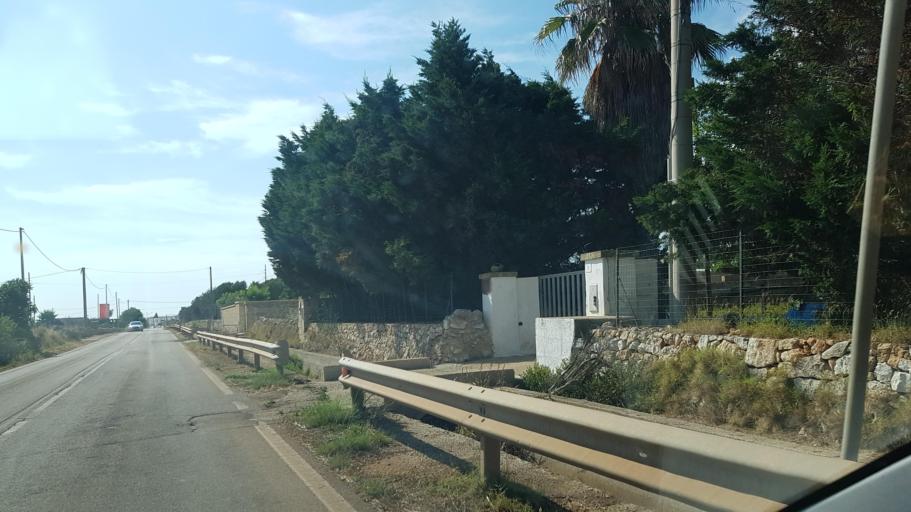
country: IT
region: Apulia
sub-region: Provincia di Lecce
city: Acquarica del Capo
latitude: 39.8422
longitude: 18.2185
